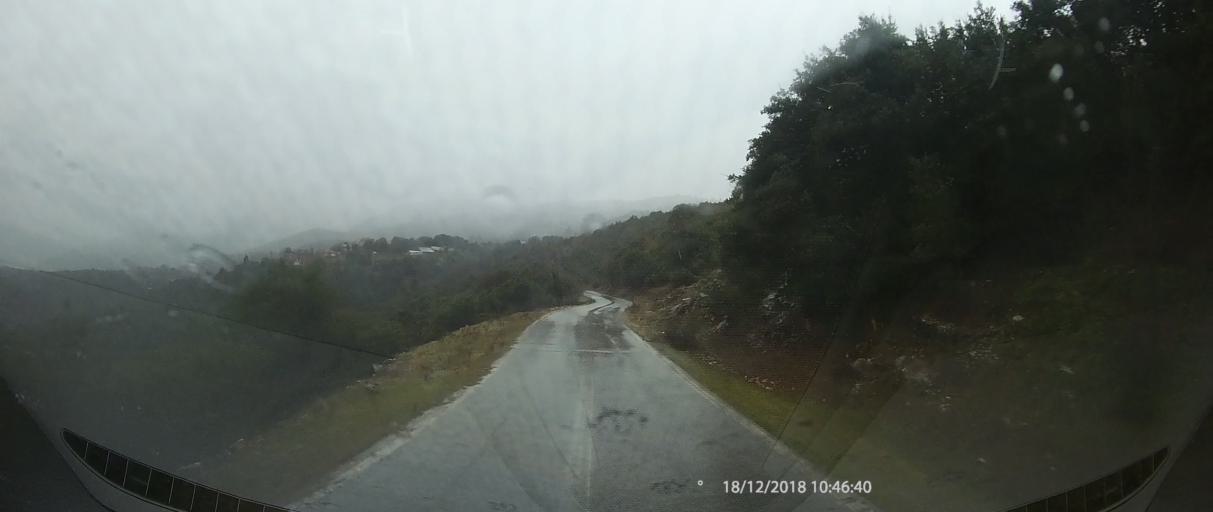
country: GR
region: Central Macedonia
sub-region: Nomos Pierias
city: Kato Milia
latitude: 40.1865
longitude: 22.3251
